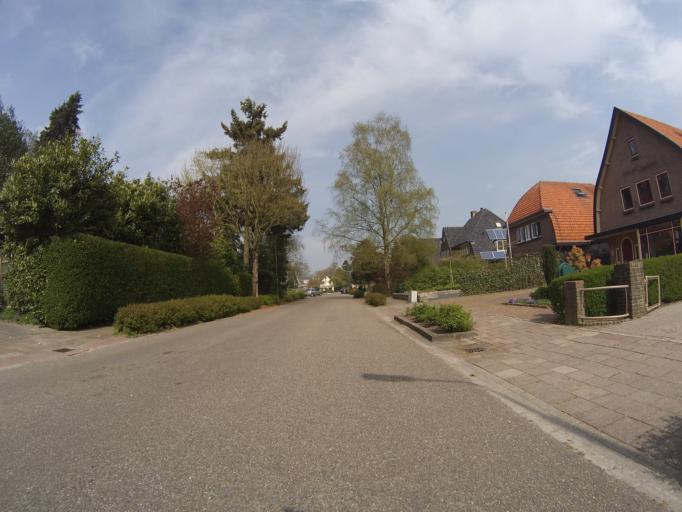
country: NL
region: Utrecht
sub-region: Gemeente Soest
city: Soest
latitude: 52.1650
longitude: 5.3159
